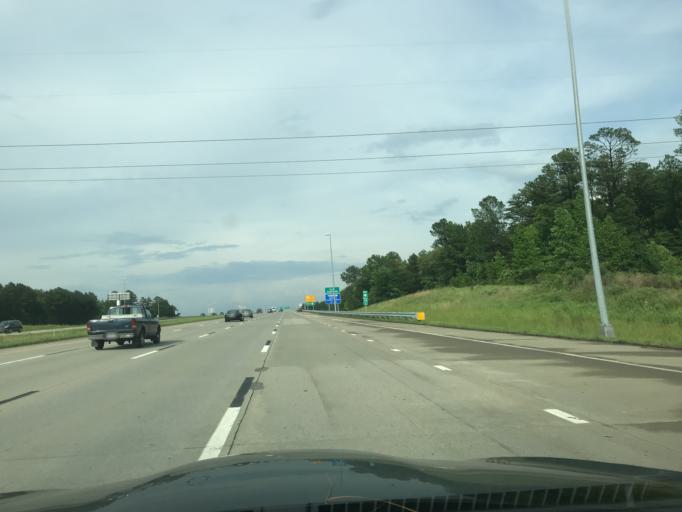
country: US
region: North Carolina
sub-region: Wake County
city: Morrisville
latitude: 35.8596
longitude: -78.8511
